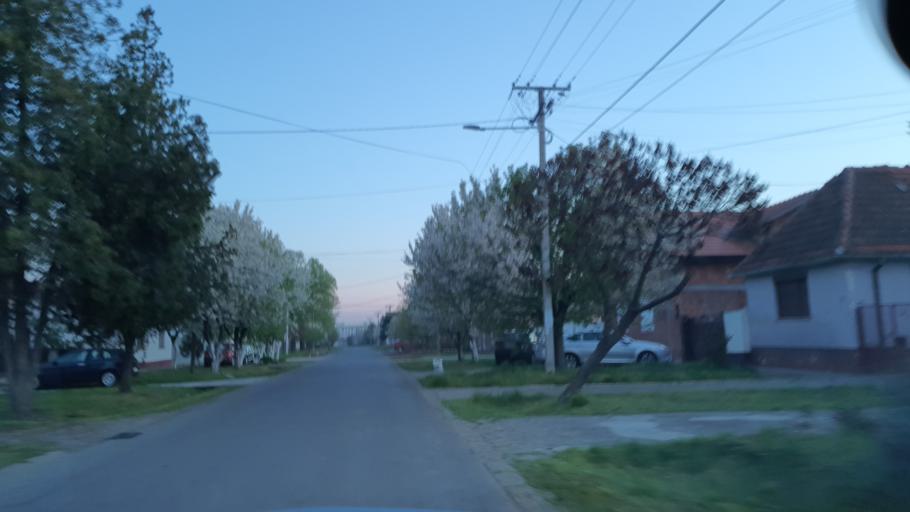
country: RS
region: Autonomna Pokrajina Vojvodina
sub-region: Sremski Okrug
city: Stara Pazova
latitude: 44.9932
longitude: 20.1595
